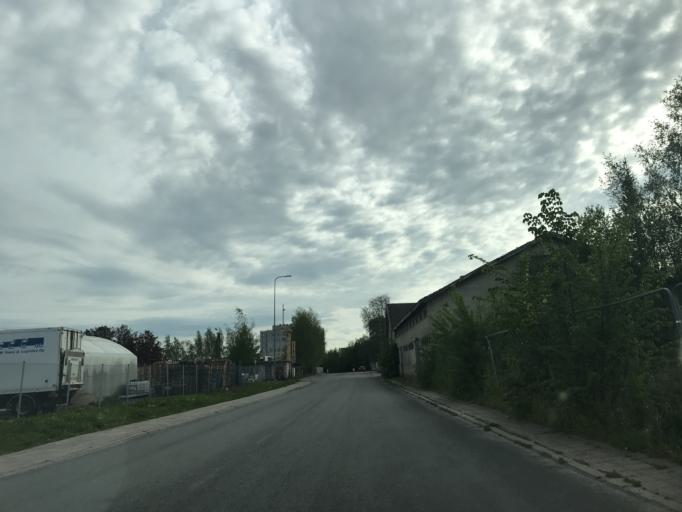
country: FI
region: Varsinais-Suomi
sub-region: Turku
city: Turku
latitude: 60.4487
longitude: 22.3077
